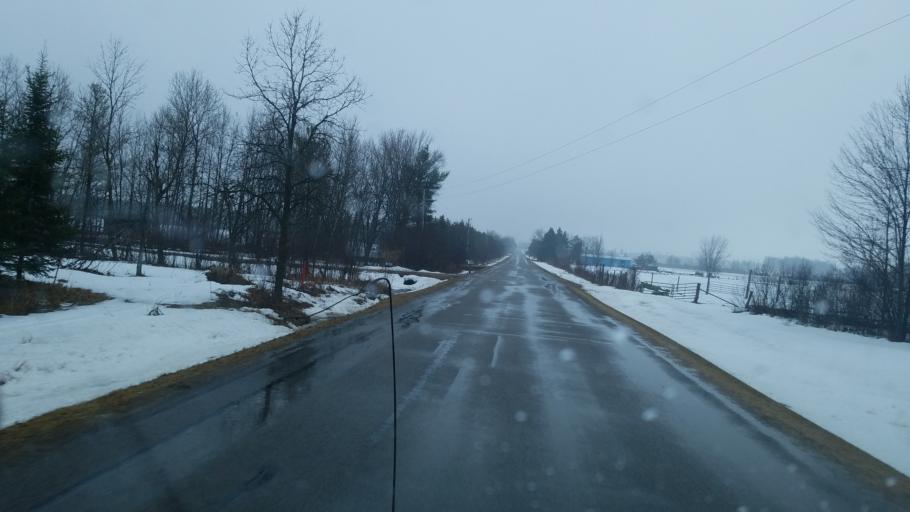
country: US
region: Wisconsin
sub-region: Marathon County
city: Spencer
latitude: 44.6730
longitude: -90.2790
